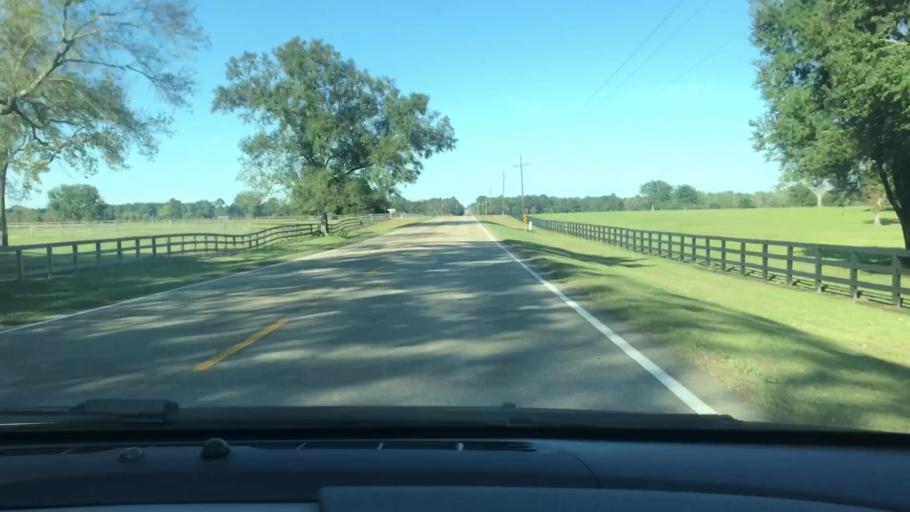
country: US
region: Louisiana
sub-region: Saint Tammany Parish
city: Abita Springs
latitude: 30.5628
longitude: -90.0412
